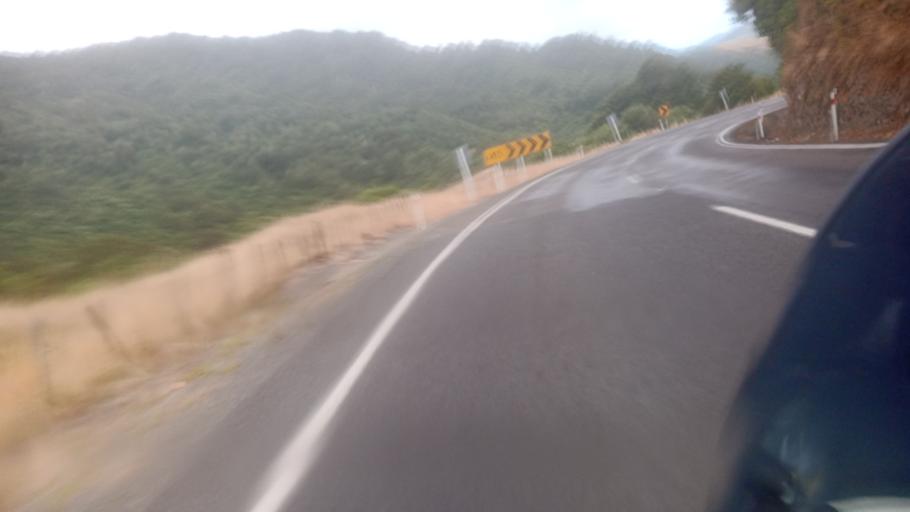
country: NZ
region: Bay of Plenty
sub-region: Opotiki District
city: Opotiki
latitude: -38.3574
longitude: 177.4530
